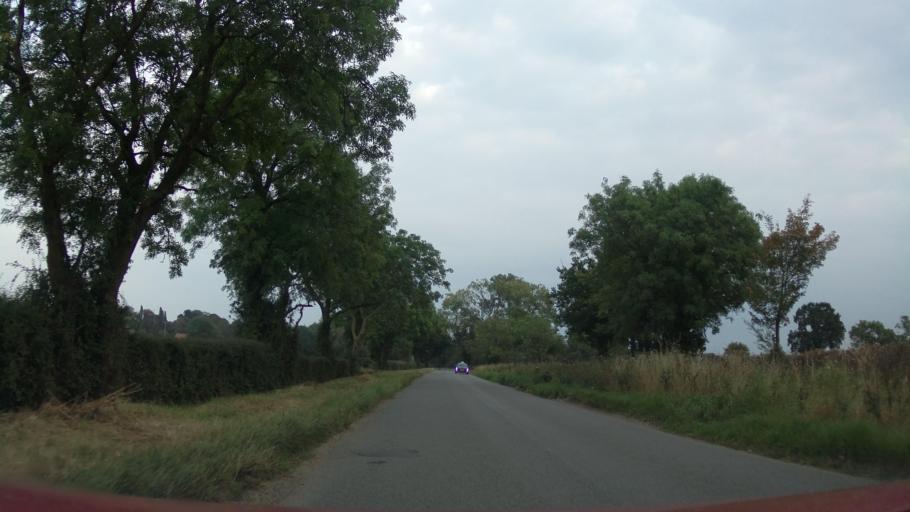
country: GB
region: England
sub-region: Lincolnshire
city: Skellingthorpe
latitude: 53.1430
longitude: -0.6517
